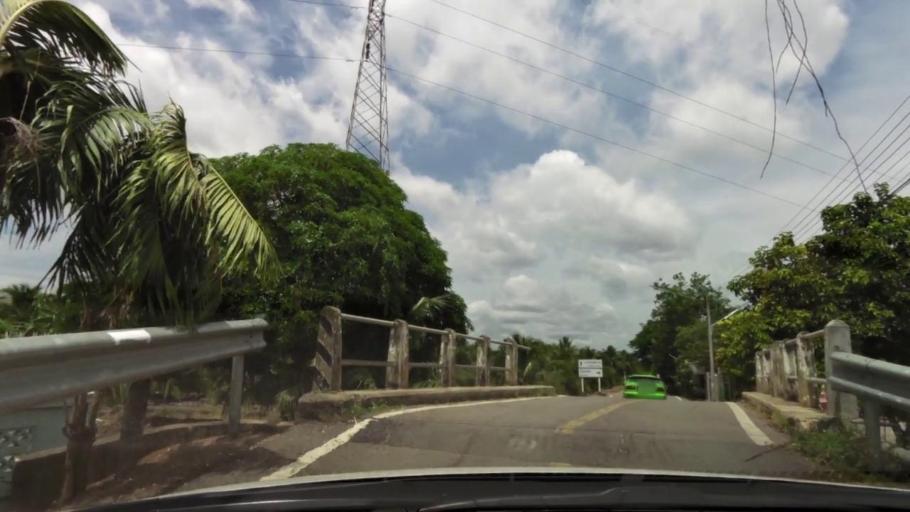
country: TH
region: Ratchaburi
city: Damnoen Saduak
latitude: 13.5181
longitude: 100.0074
